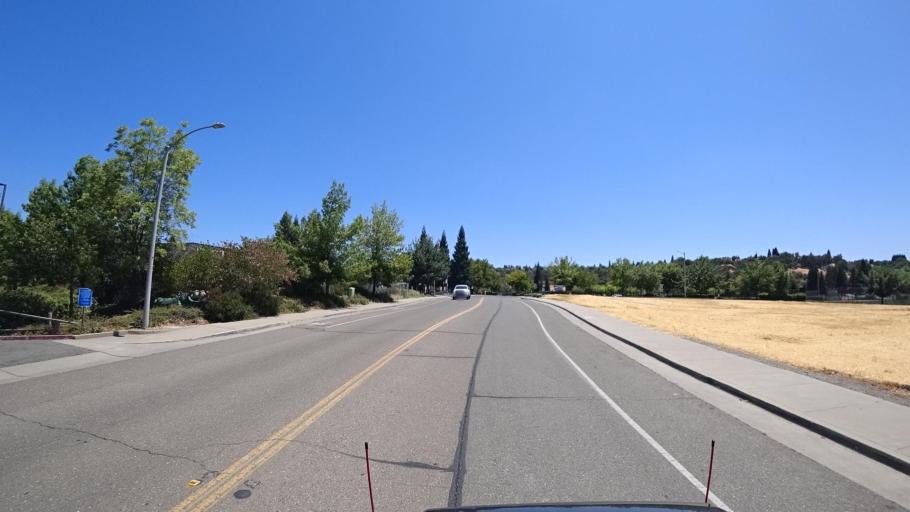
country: US
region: California
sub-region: Placer County
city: Rocklin
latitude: 38.8152
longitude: -121.2545
